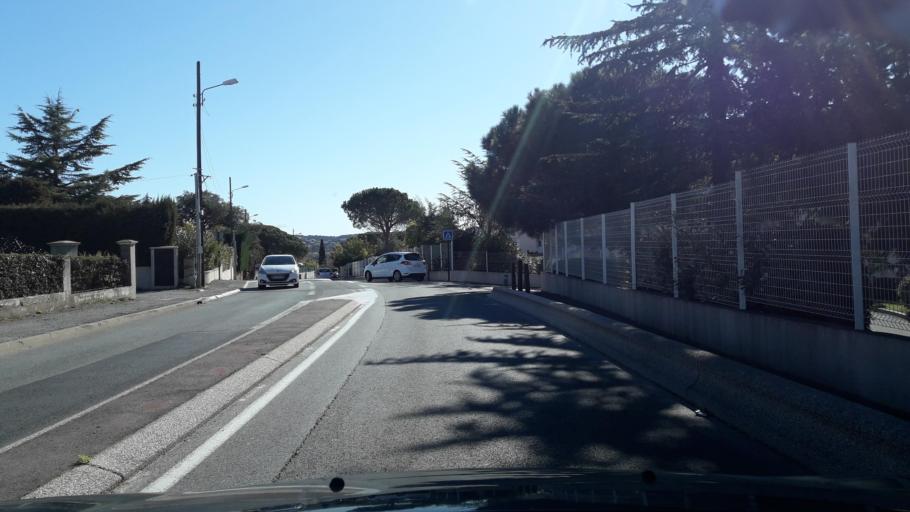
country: FR
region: Provence-Alpes-Cote d'Azur
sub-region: Departement du Var
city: Frejus
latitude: 43.4415
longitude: 6.7538
